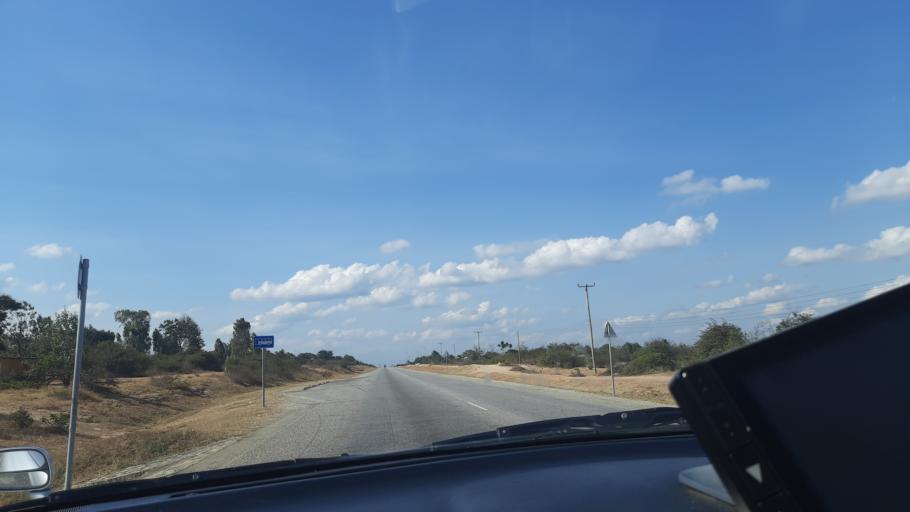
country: TZ
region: Singida
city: Itigi
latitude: -5.5501
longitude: 34.6647
